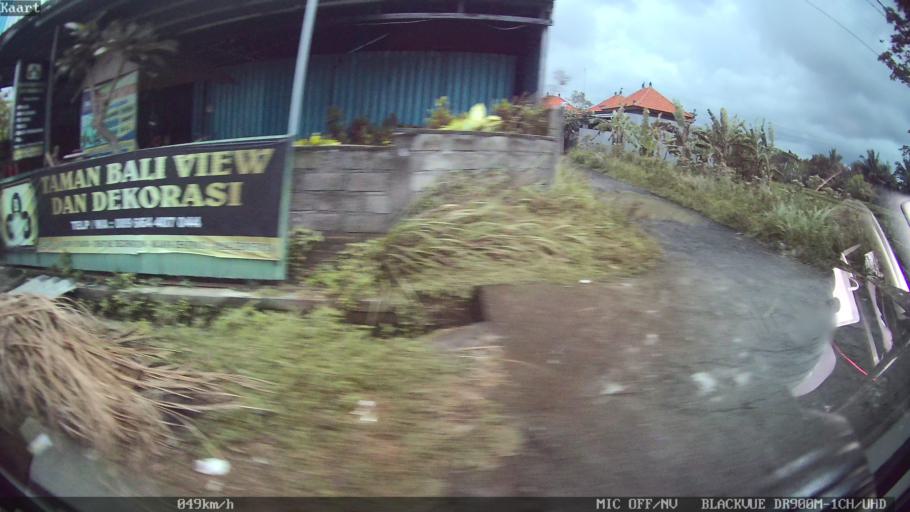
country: ID
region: Bali
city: Banjar Serangan
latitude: -8.5338
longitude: 115.1786
